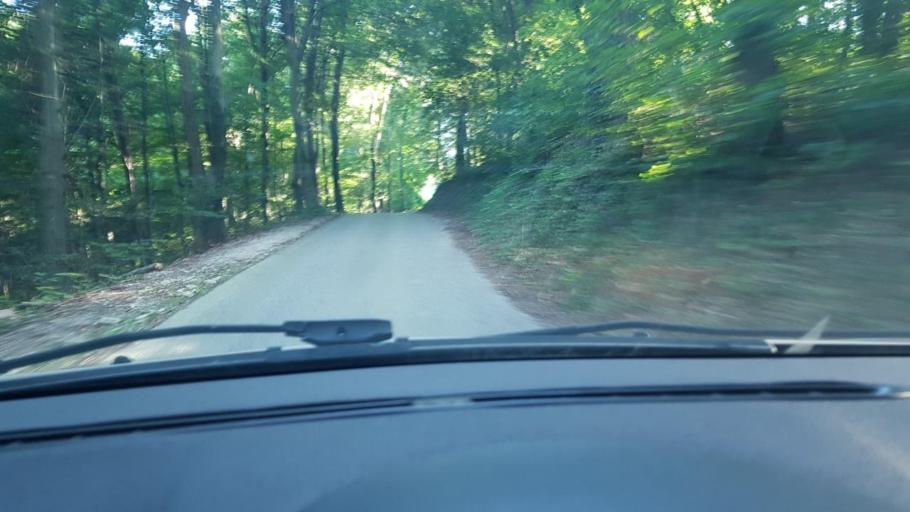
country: HR
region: Krapinsko-Zagorska
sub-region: Grad Krapina
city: Krapina
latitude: 46.1209
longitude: 15.8514
